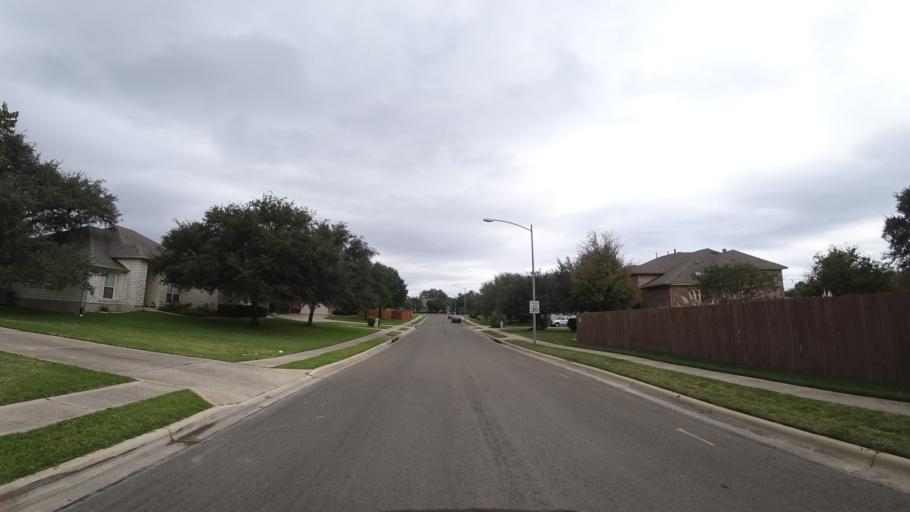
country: US
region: Texas
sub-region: Travis County
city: Shady Hollow
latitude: 30.1537
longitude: -97.8594
